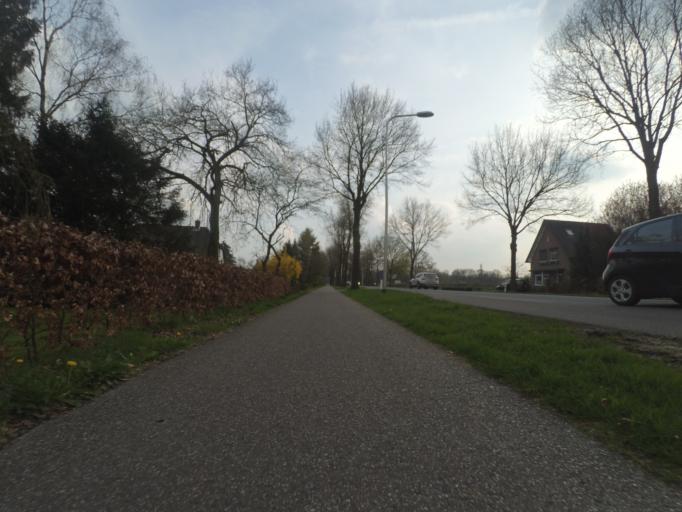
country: NL
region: Gelderland
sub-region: Gemeente Apeldoorn
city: Beekbergen
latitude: 52.1680
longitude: 5.9622
